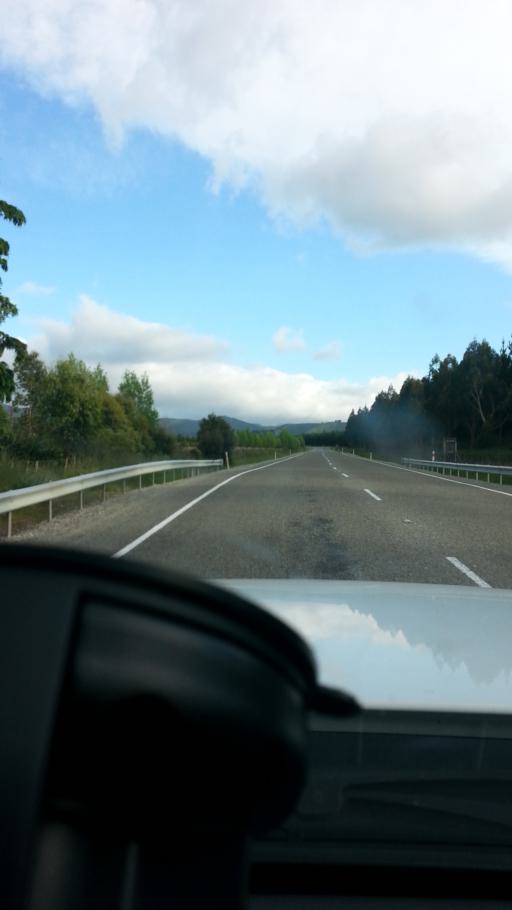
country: NZ
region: Wellington
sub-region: Masterton District
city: Masterton
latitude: -40.8074
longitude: 175.6200
